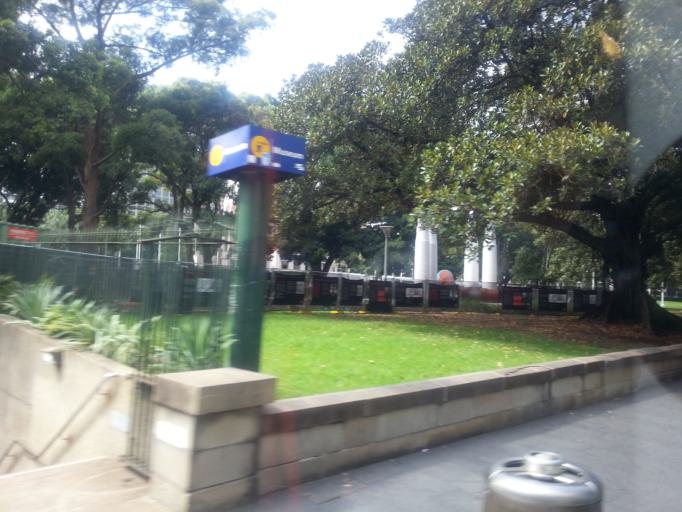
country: AU
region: New South Wales
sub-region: City of Sydney
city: Haymarket
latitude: -33.8749
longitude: 151.2102
